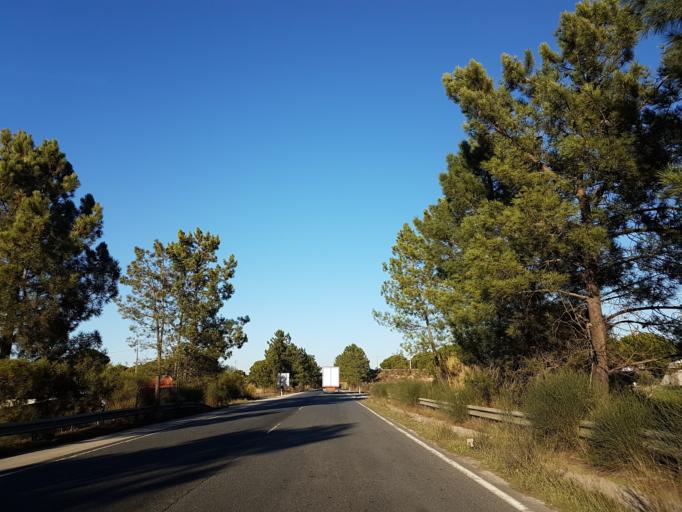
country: PT
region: Setubal
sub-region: Alcacer do Sal
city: Alcacer do Sal
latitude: 38.3933
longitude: -8.5210
